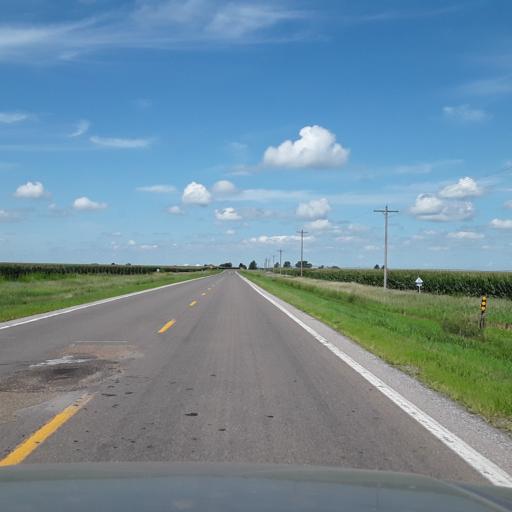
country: US
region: Nebraska
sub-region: Polk County
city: Osceola
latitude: 41.0760
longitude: -97.4142
